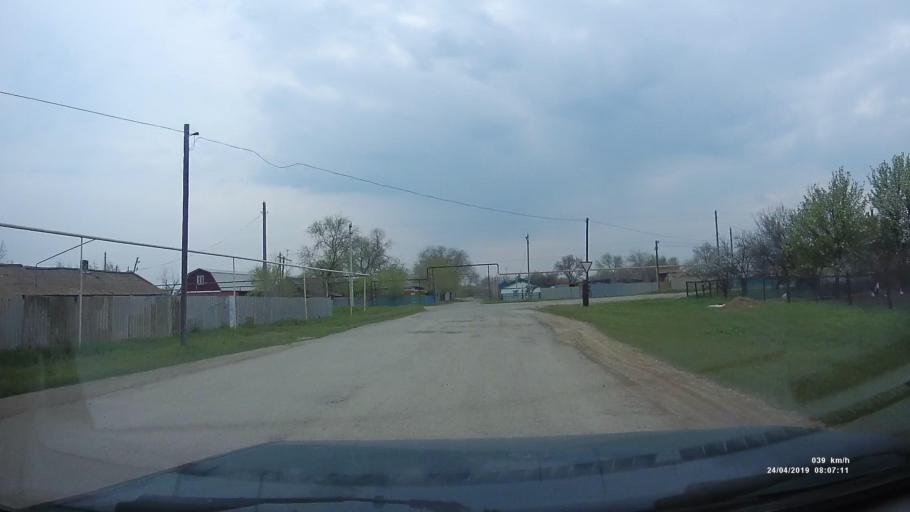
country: RU
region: Kalmykiya
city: Priyutnoye
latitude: 46.1018
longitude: 43.4984
